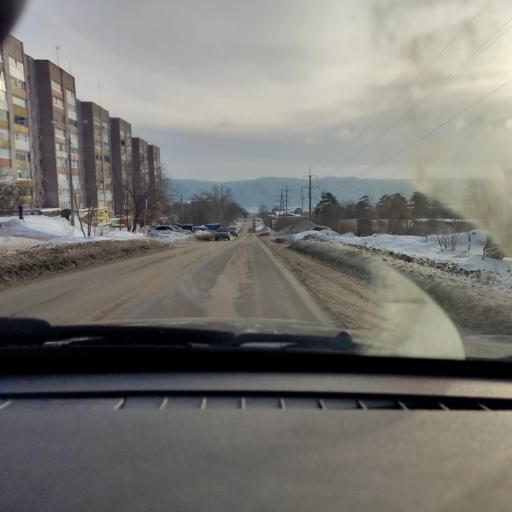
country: RU
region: Samara
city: Pribrezhnyy
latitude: 53.4914
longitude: 49.8473
